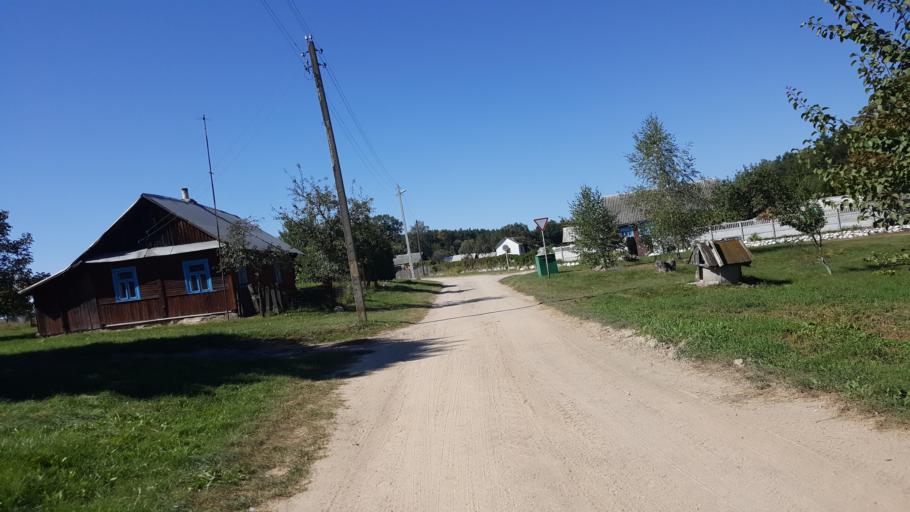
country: PL
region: Lublin Voivodeship
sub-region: Powiat bialski
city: Rokitno
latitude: 52.2235
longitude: 23.3426
